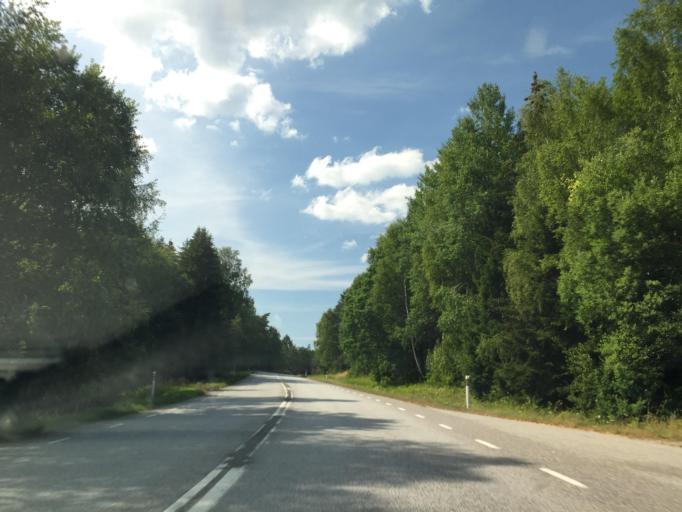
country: SE
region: Vaestra Goetaland
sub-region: Tanums Kommun
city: Grebbestad
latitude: 58.8222
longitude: 11.2562
